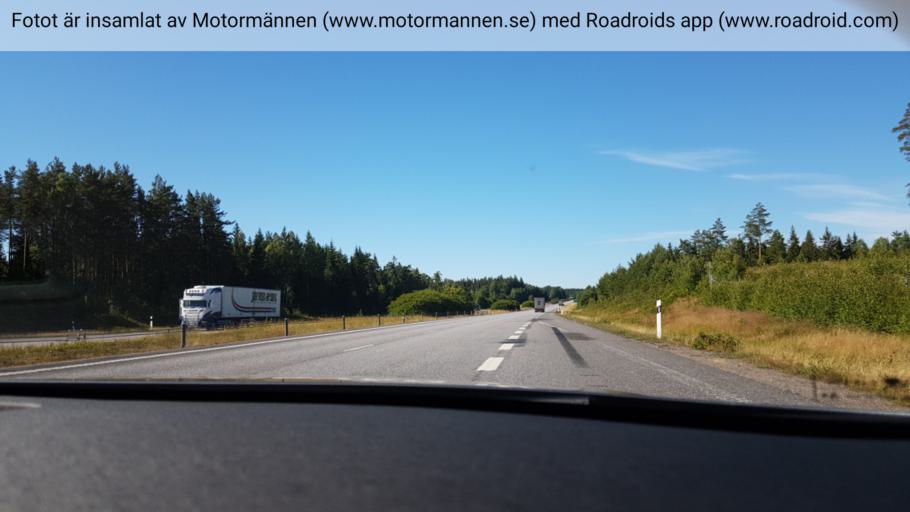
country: SE
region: Joenkoeping
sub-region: Varnamo Kommun
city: Varnamo
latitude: 57.2005
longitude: 14.0819
